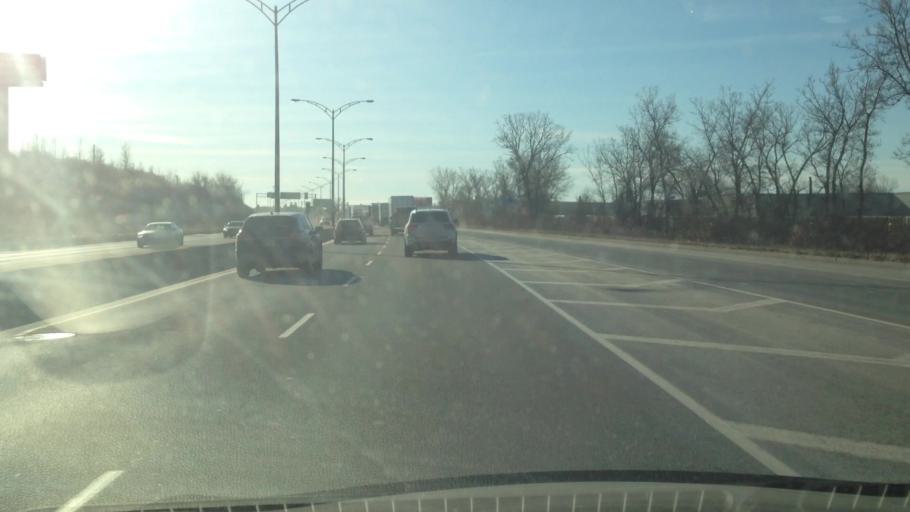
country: CA
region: Quebec
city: Cote-Saint-Luc
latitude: 45.4587
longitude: -73.6971
